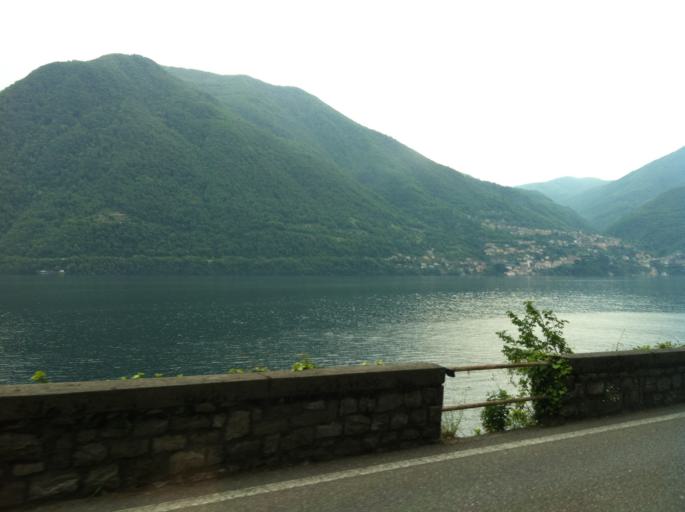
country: IT
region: Lombardy
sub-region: Provincia di Como
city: Argegno
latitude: 45.9290
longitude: 9.1300
